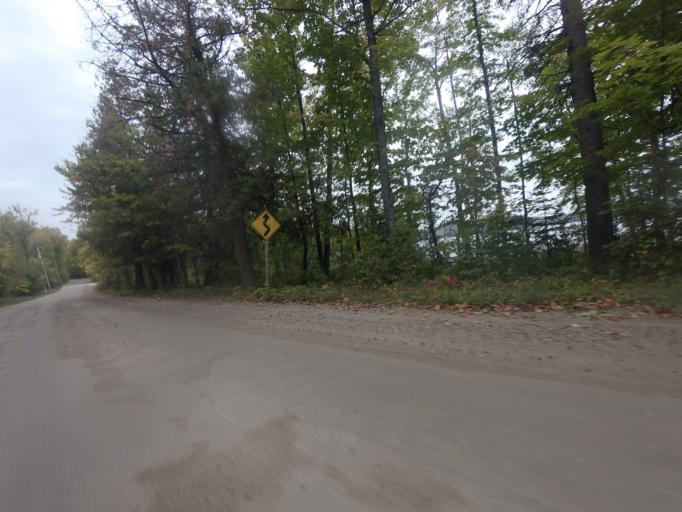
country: CA
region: Quebec
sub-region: Outaouais
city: Maniwaki
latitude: 46.0356
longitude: -75.9363
